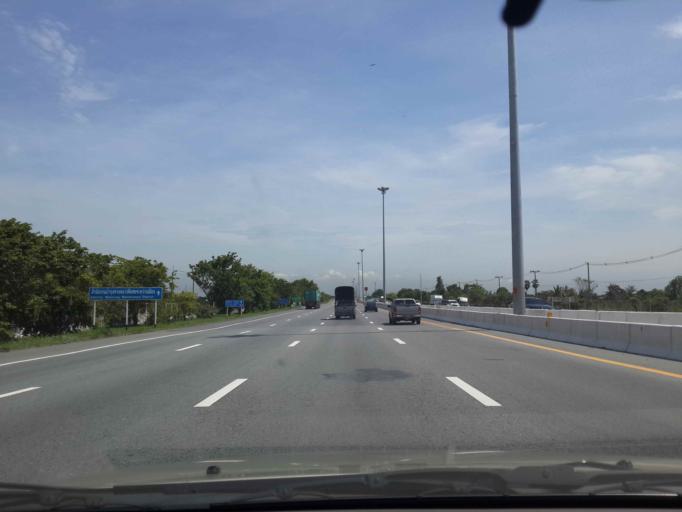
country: TH
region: Samut Prakan
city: Ban Khlong Bang Sao Thong
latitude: 13.6836
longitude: 100.8331
